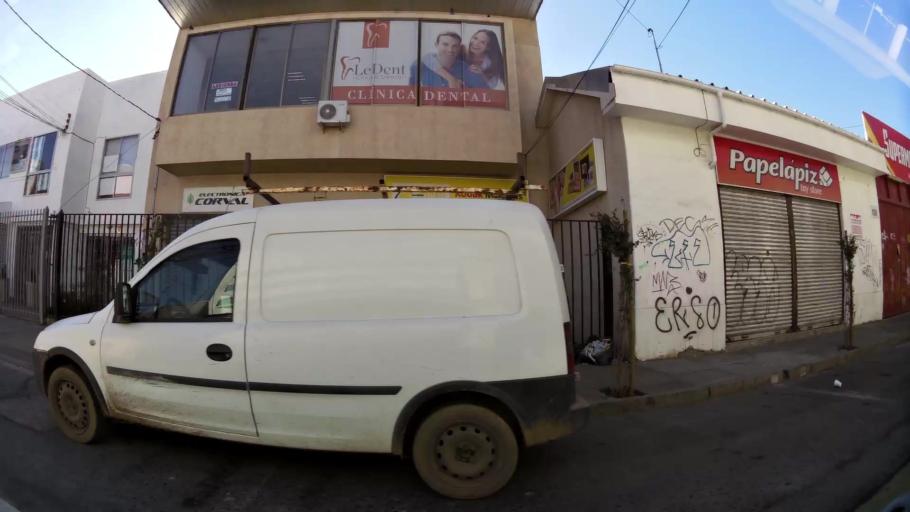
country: CL
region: O'Higgins
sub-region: Provincia de Cachapoal
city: Rancagua
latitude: -34.1668
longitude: -70.7429
